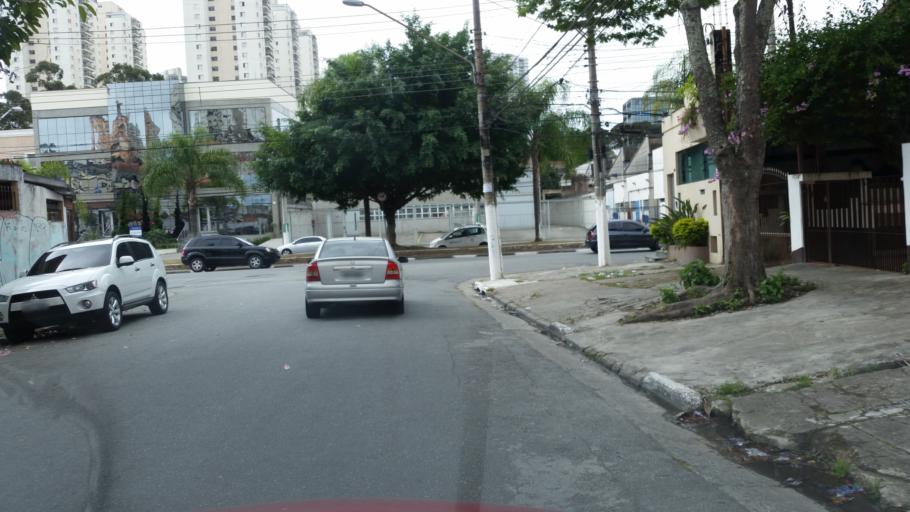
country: BR
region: Sao Paulo
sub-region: Diadema
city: Diadema
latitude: -23.6621
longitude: -46.6883
